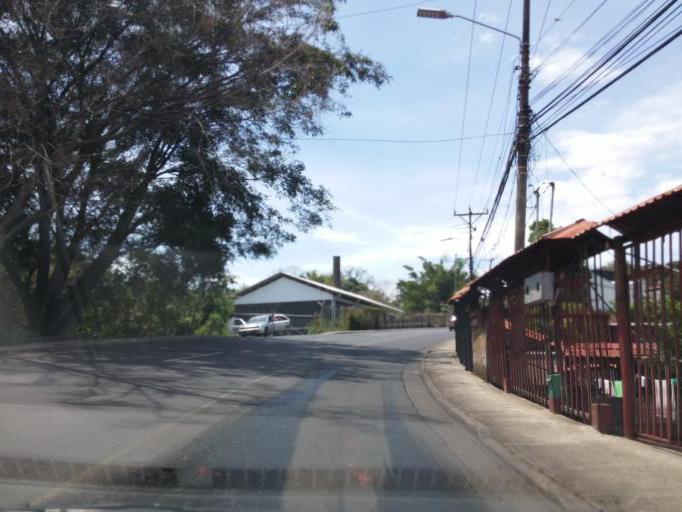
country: CR
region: Alajuela
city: Alajuela
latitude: 10.0032
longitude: -84.2019
